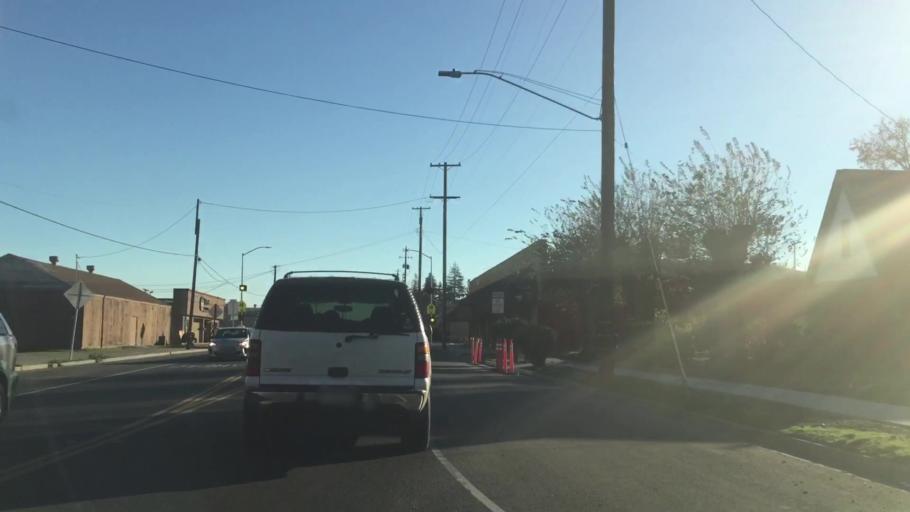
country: US
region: California
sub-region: Yuba County
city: Marysville
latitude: 39.1538
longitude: -121.5879
